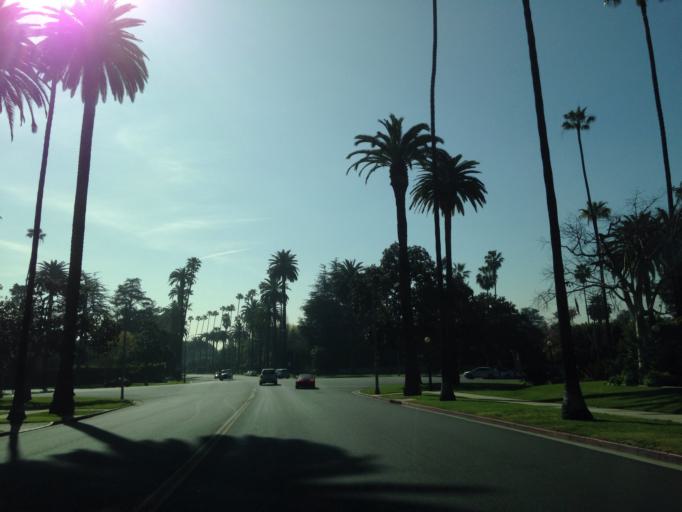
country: US
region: California
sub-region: Los Angeles County
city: Beverly Hills
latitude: 34.0806
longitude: -118.4119
